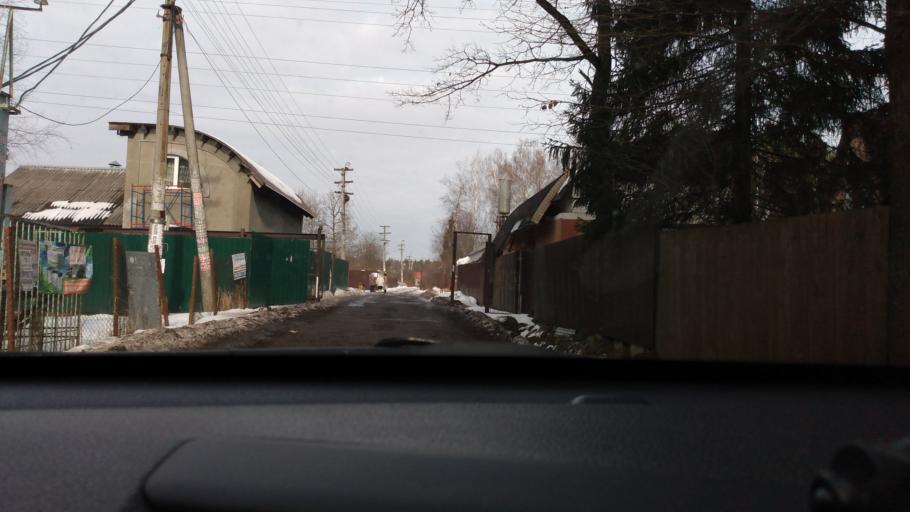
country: RU
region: Moskovskaya
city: Dedovsk
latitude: 55.8989
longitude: 37.1520
